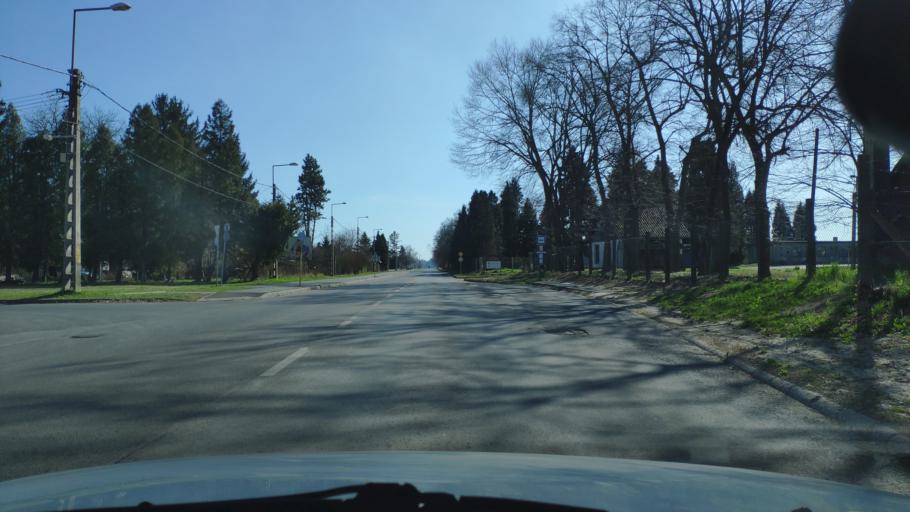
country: HU
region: Zala
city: Nagykanizsa
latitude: 46.4282
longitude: 16.9868
